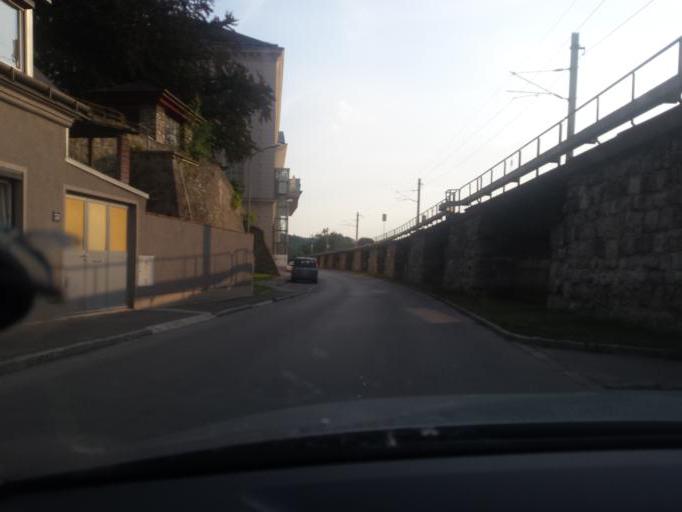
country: AT
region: Lower Austria
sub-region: Politischer Bezirk Bruck an der Leitha
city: Hainburg an der Donau
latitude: 48.1482
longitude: 16.9382
